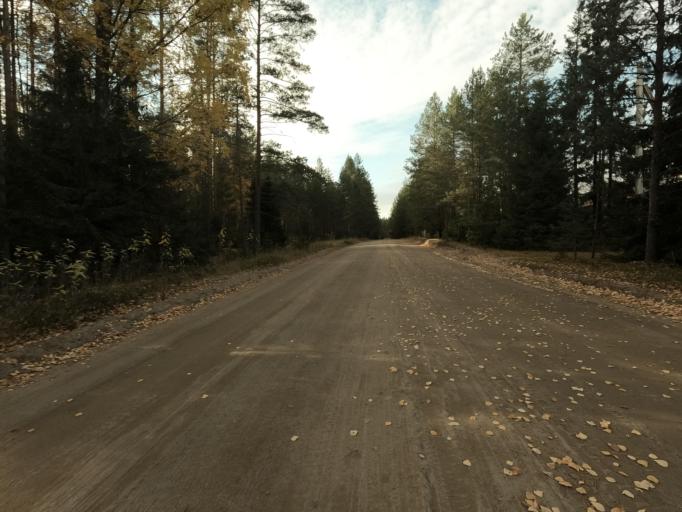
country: RU
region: Leningrad
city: Priladozhskiy
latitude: 59.6305
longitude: 31.3946
